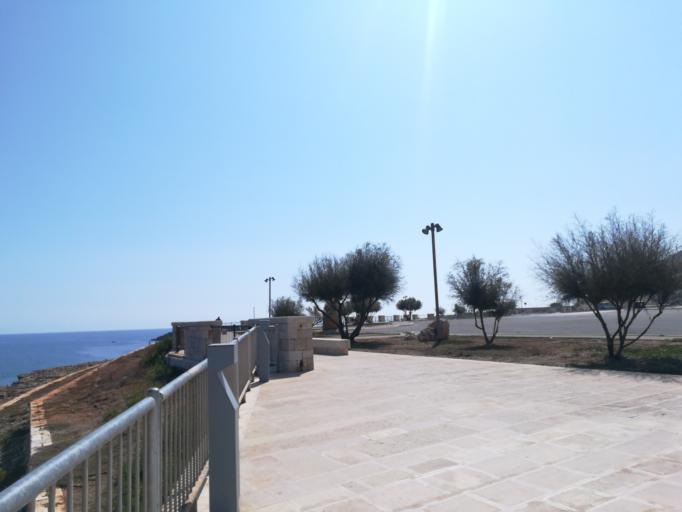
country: IT
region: Apulia
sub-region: Provincia di Bari
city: Polignano a Mare
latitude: 40.9957
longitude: 17.2273
